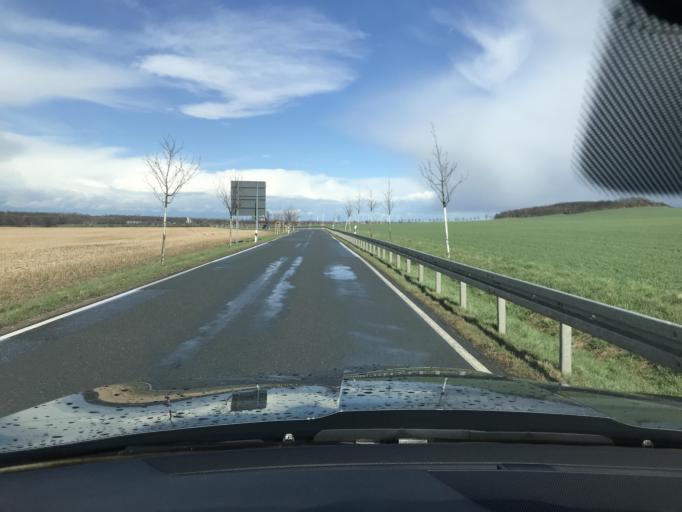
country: DE
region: Saxony-Anhalt
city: Hoym
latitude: 51.7137
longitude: 11.3076
